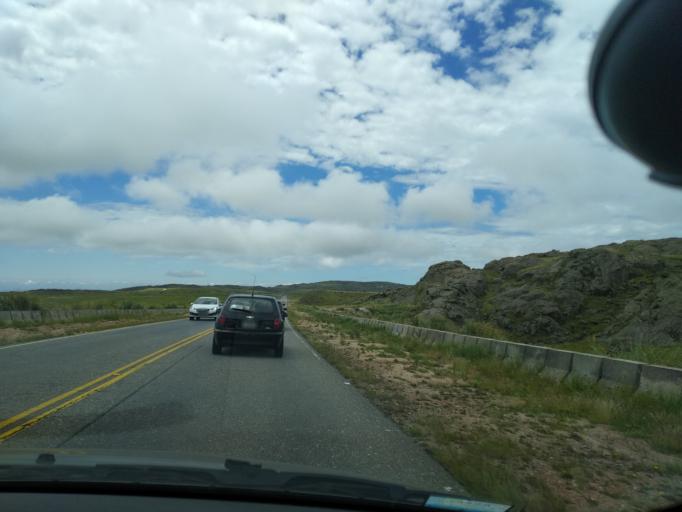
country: AR
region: Cordoba
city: Cuesta Blanca
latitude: -31.6085
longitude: -64.7253
